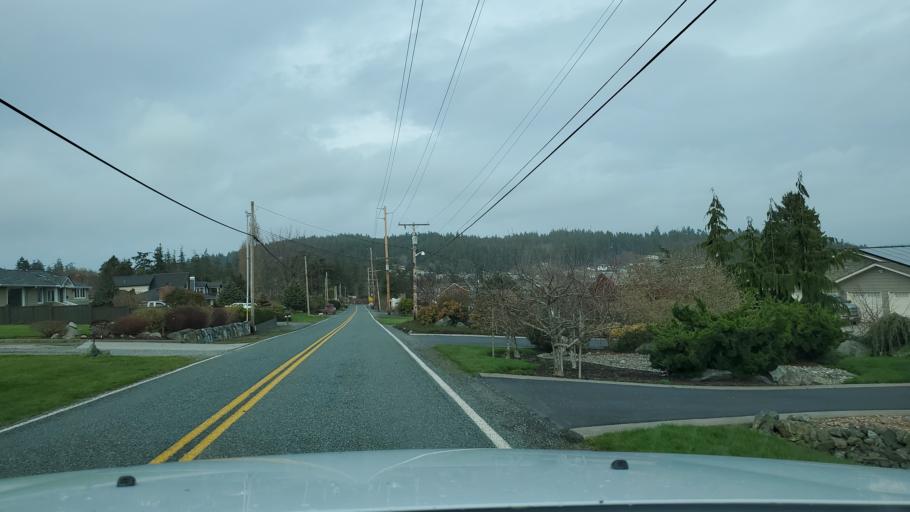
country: US
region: Washington
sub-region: Skagit County
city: Anacortes
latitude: 48.4203
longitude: -122.6146
